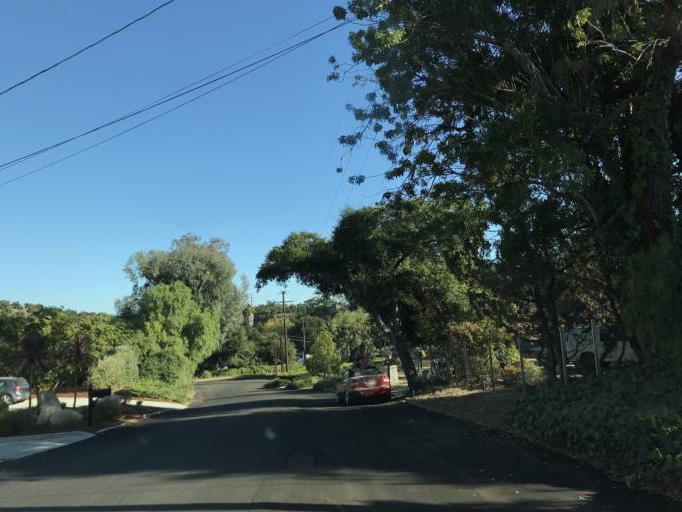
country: US
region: California
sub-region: Santa Barbara County
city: Goleta
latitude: 34.4602
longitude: -119.8171
